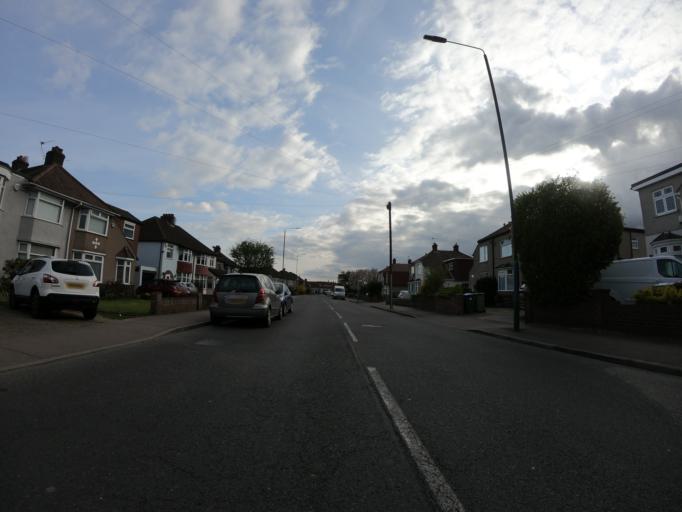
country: GB
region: England
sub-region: Greater London
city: Bexleyheath
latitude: 51.4690
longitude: 0.1432
